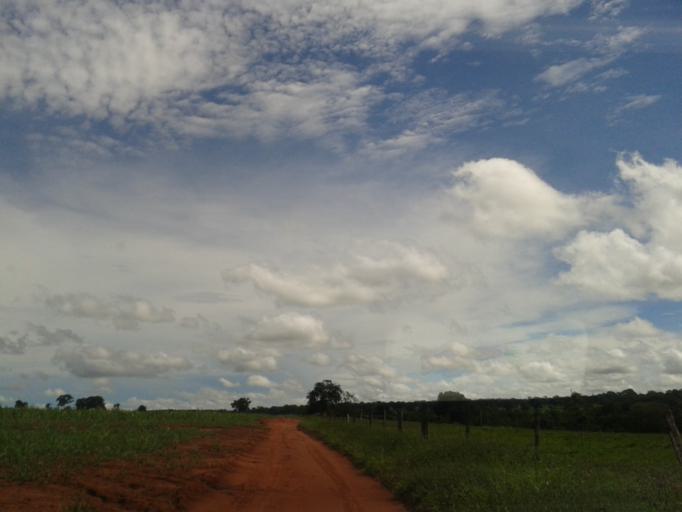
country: BR
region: Minas Gerais
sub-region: Santa Vitoria
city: Santa Vitoria
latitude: -19.1363
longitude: -50.4866
